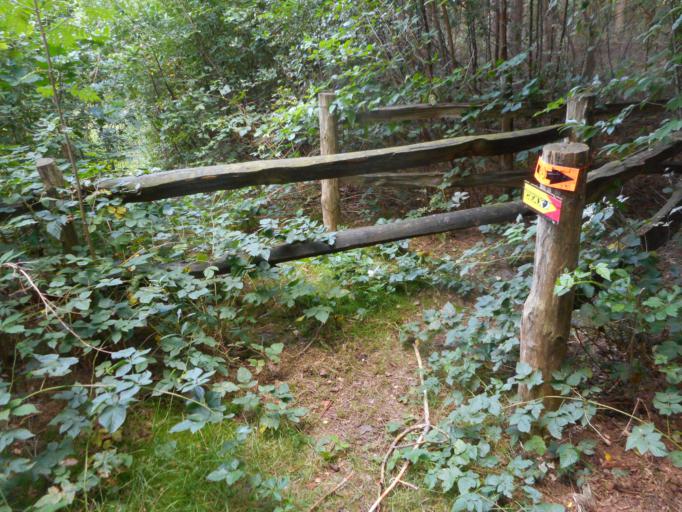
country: BE
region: Flanders
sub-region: Provincie Antwerpen
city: Lille
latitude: 51.2719
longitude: 4.8069
